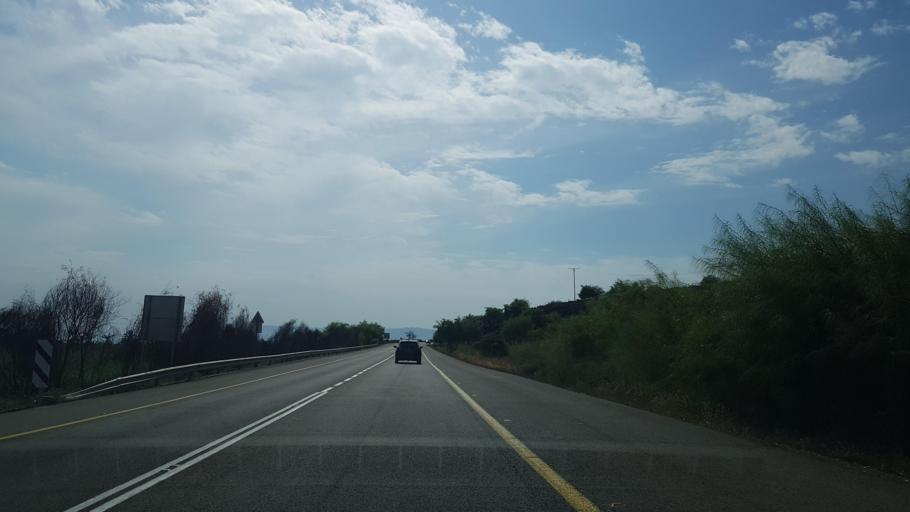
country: SY
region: Quneitra
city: Al Butayhah
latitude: 32.9003
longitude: 35.6110
